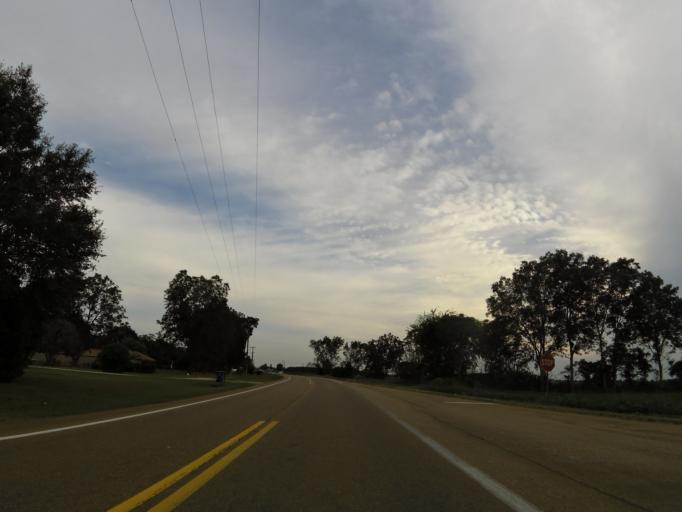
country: US
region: Alabama
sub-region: Monroe County
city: Frisco City
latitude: 31.4122
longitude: -87.4288
